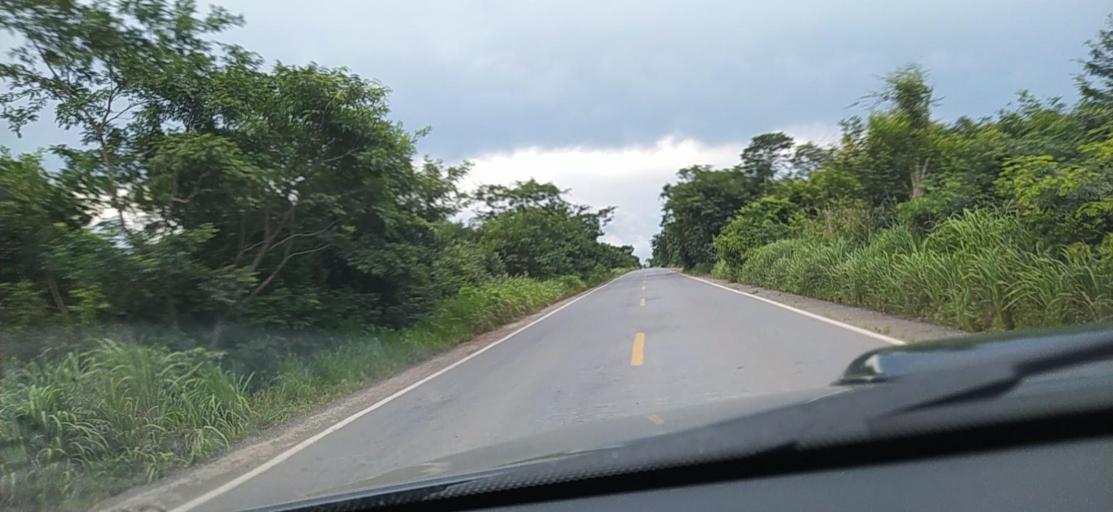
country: BR
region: Minas Gerais
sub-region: Francisco Sa
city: Francisco Sa
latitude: -16.2519
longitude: -43.6329
